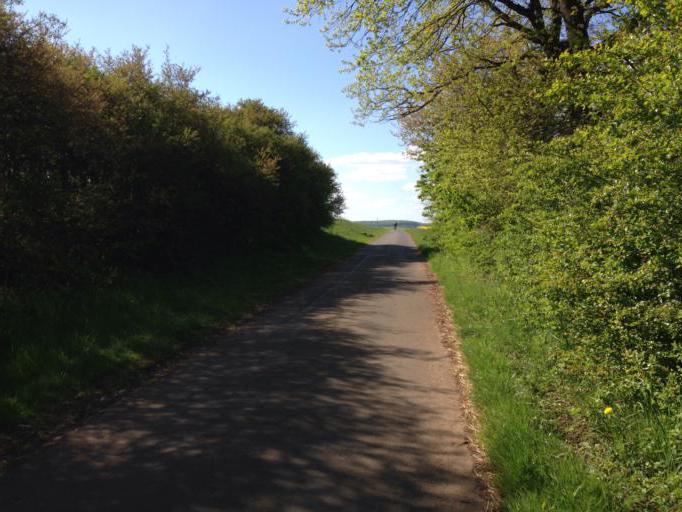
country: DE
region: Hesse
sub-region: Regierungsbezirk Giessen
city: Reiskirchen
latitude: 50.5599
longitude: 8.8903
